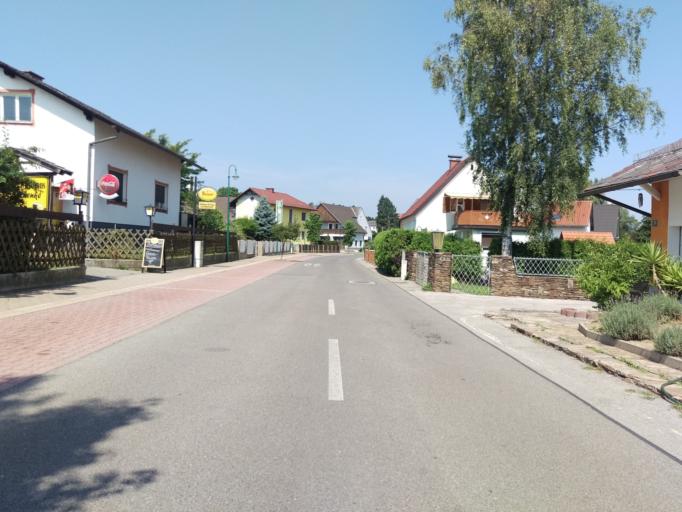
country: AT
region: Styria
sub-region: Politischer Bezirk Graz-Umgebung
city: Kalsdorf bei Graz
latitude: 46.9614
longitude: 15.4824
